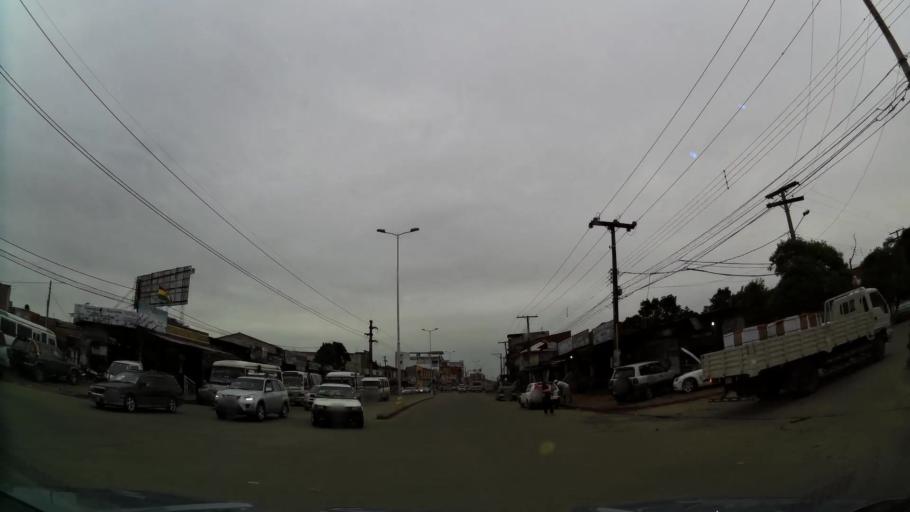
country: BO
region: Santa Cruz
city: Santa Cruz de la Sierra
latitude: -17.8126
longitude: -63.1860
